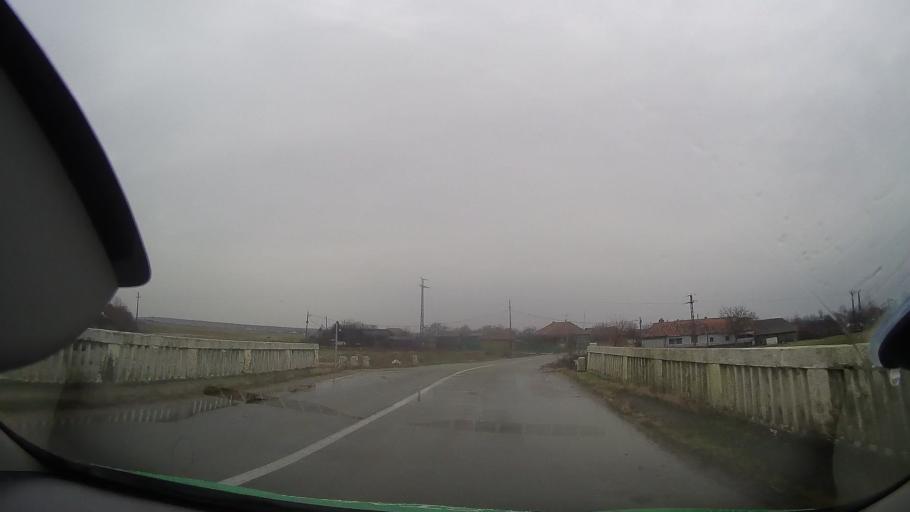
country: RO
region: Bihor
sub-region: Comuna Tinca
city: Gurbediu
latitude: 46.7826
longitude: 21.8680
